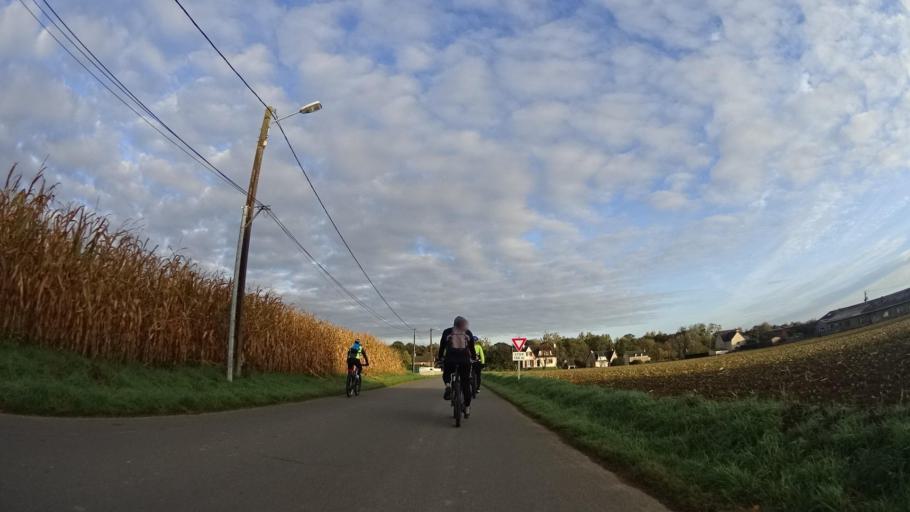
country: FR
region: Brittany
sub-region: Departement des Cotes-d'Armor
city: Evran
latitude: 48.3795
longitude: -1.9693
